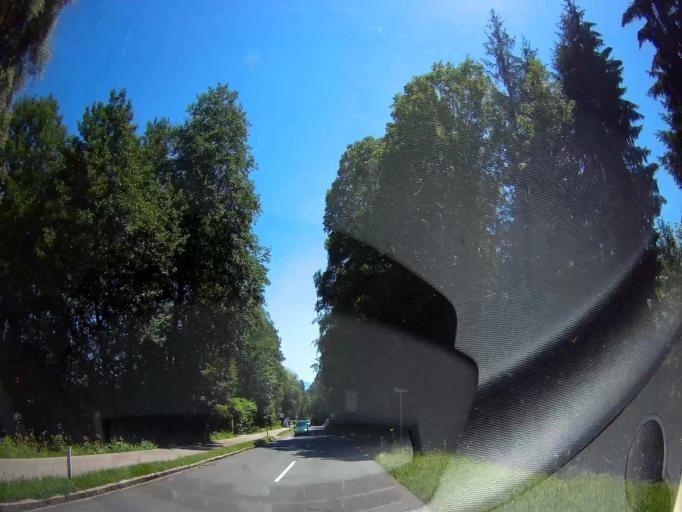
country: AT
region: Carinthia
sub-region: Politischer Bezirk Klagenfurt Land
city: Kottmannsdorf
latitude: 46.6074
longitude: 14.2512
